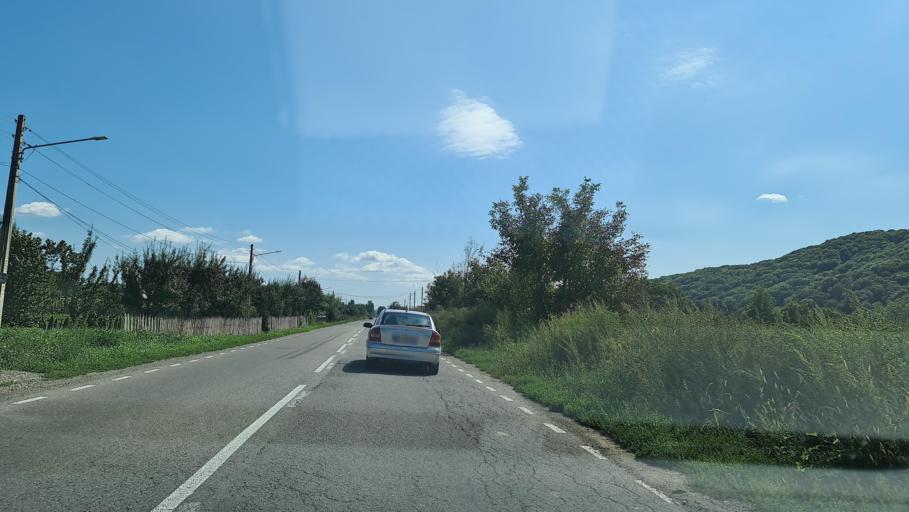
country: RO
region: Neamt
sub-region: Comuna Tazlau
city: Tazlau
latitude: 46.7094
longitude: 26.4862
